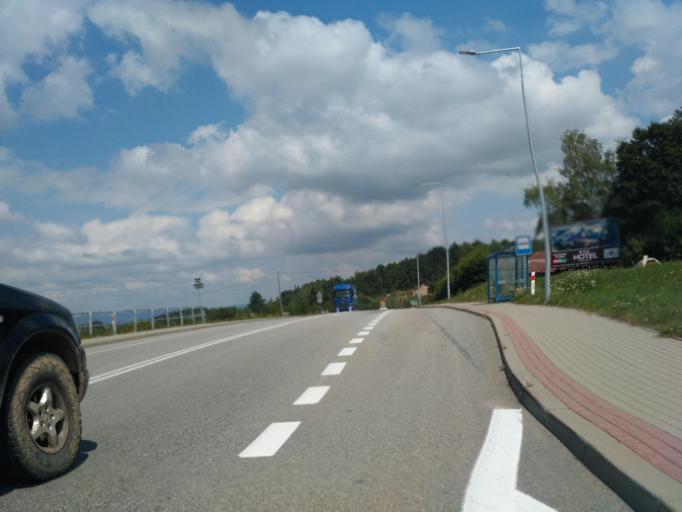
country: PL
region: Subcarpathian Voivodeship
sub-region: Powiat krosnienski
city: Dukla
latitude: 49.6037
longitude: 21.7282
